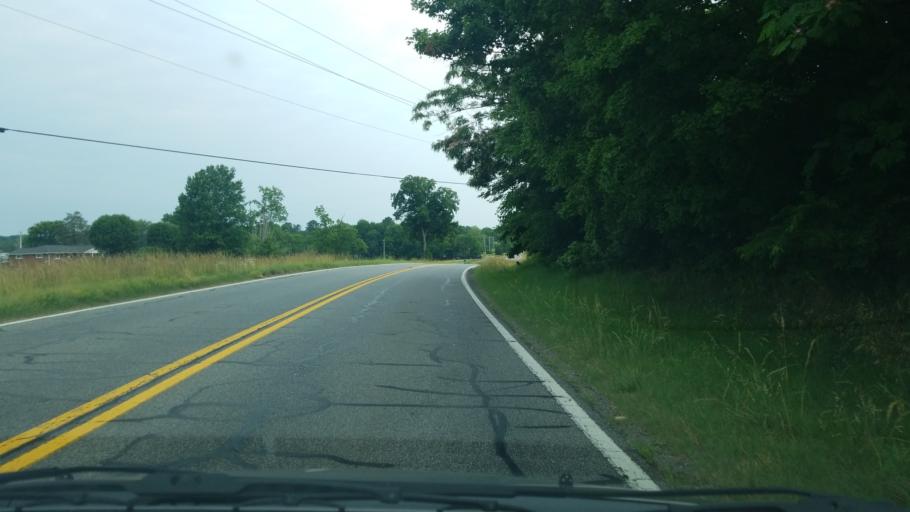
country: US
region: Georgia
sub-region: Catoosa County
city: Ringgold
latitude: 34.8576
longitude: -85.1439
